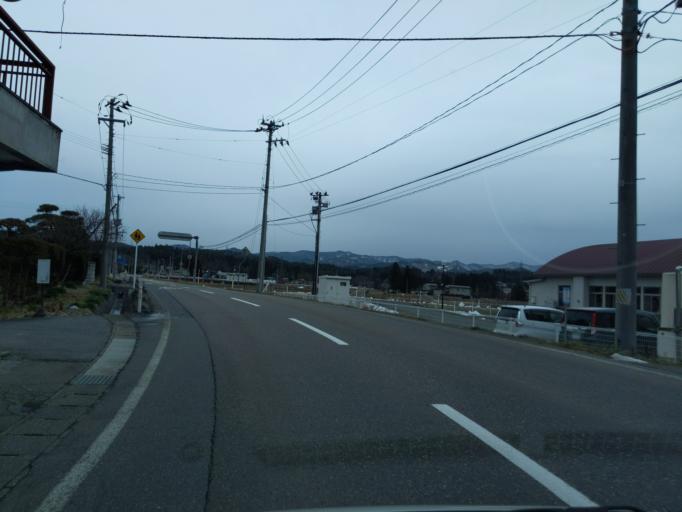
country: JP
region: Iwate
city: Mizusawa
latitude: 39.1606
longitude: 141.1969
